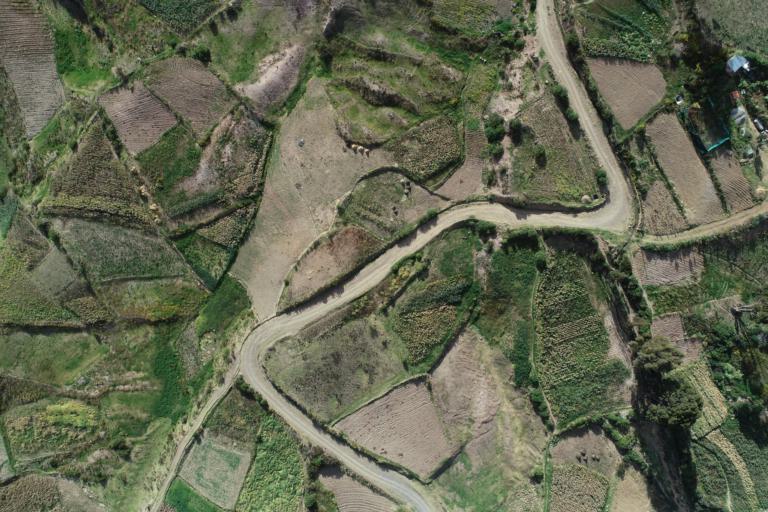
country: BO
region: La Paz
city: La Paz
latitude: -16.5526
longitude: -67.9907
